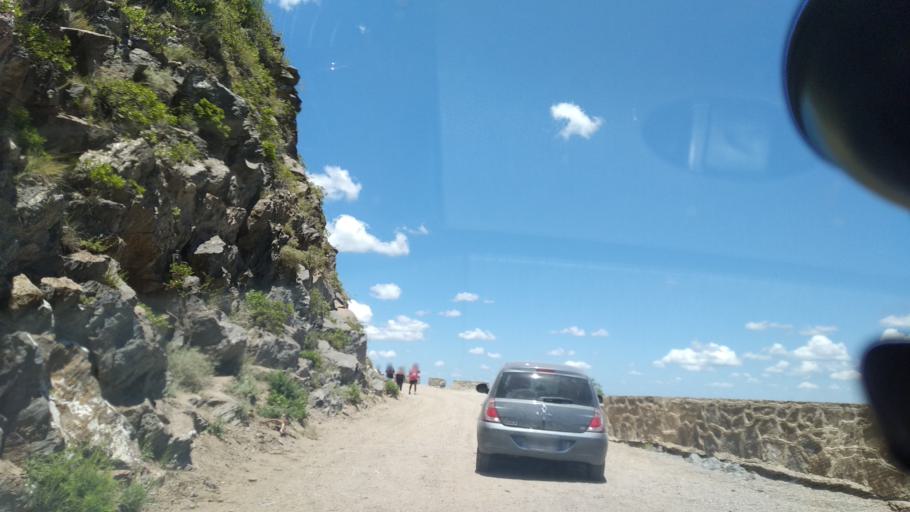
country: AR
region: Cordoba
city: Salsacate
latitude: -31.3756
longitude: -65.4080
